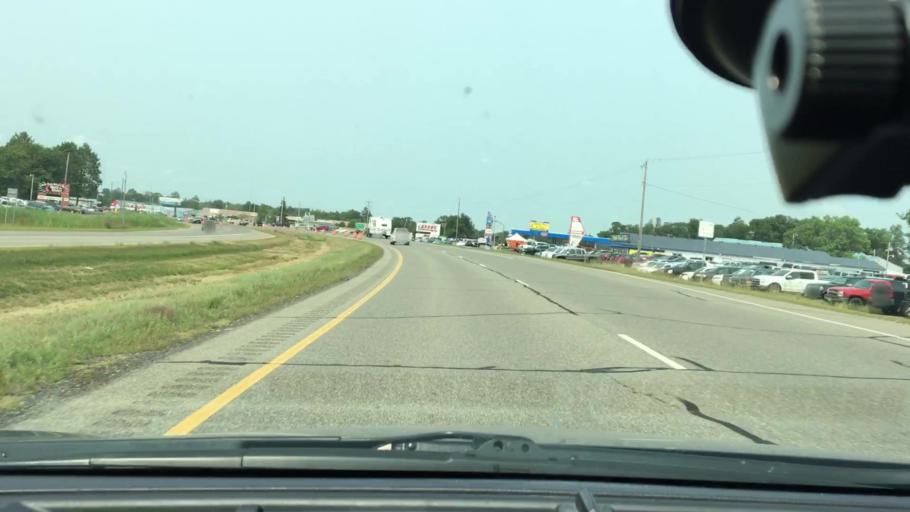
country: US
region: Minnesota
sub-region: Cass County
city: East Gull Lake
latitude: 46.4146
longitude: -94.2856
